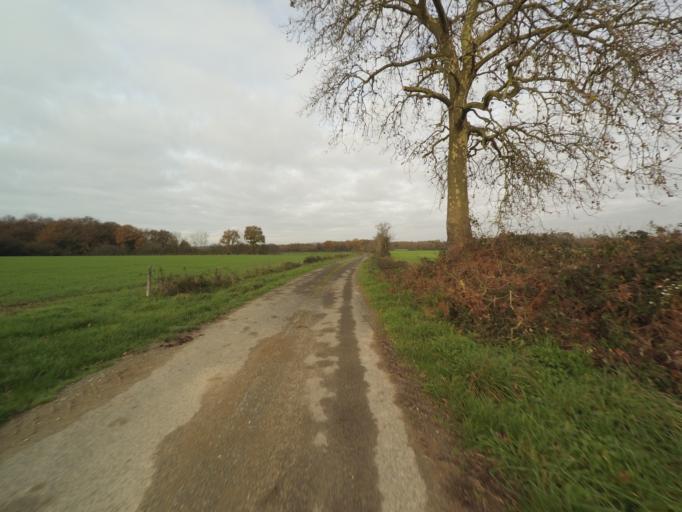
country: FR
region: Pays de la Loire
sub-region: Departement de la Loire-Atlantique
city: La Planche
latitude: 47.0123
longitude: -1.3932
